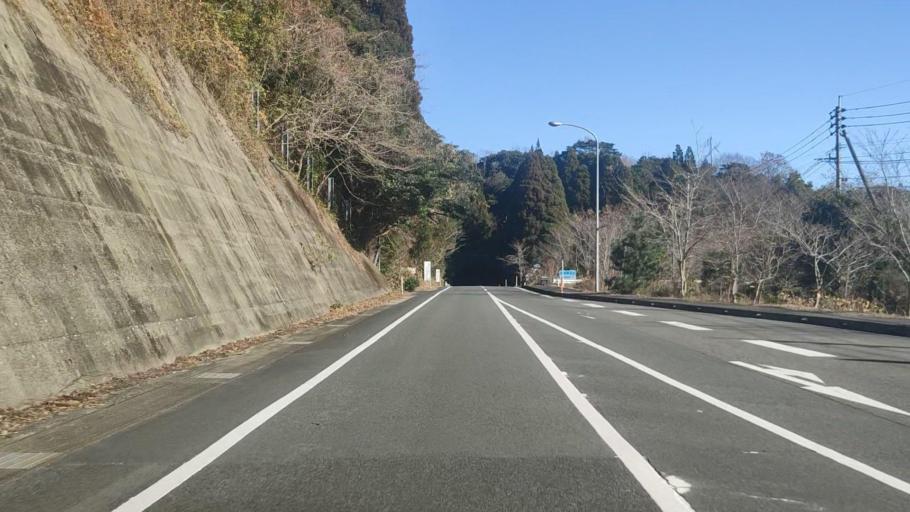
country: JP
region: Miyazaki
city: Nobeoka
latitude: 32.6967
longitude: 131.8127
